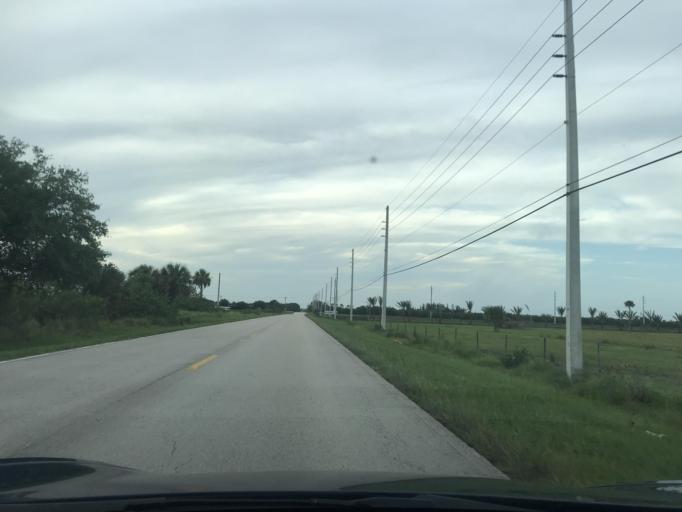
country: US
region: Florida
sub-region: Indian River County
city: West Vero Corridor
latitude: 27.6053
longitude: -80.4962
